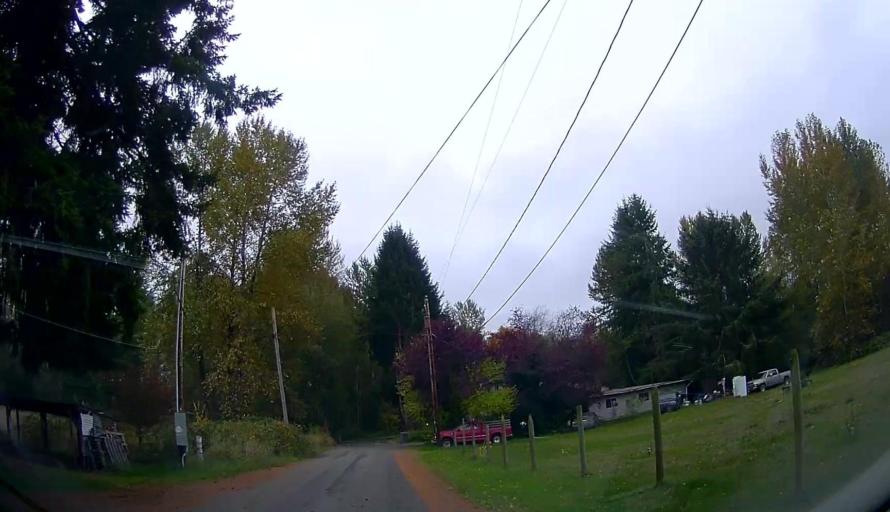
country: US
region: Washington
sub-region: Skagit County
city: Sedro-Woolley
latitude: 48.5232
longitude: -122.0882
